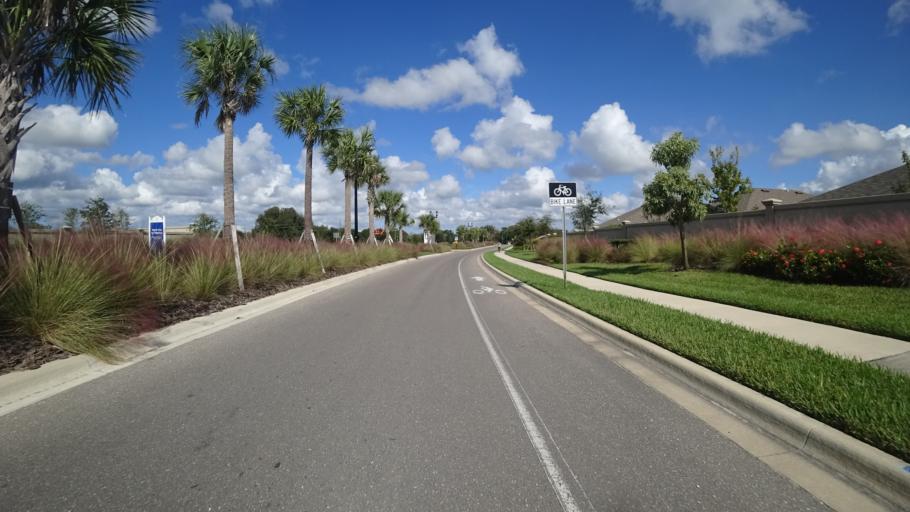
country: US
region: Florida
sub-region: Manatee County
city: Ellenton
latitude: 27.5718
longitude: -82.5079
